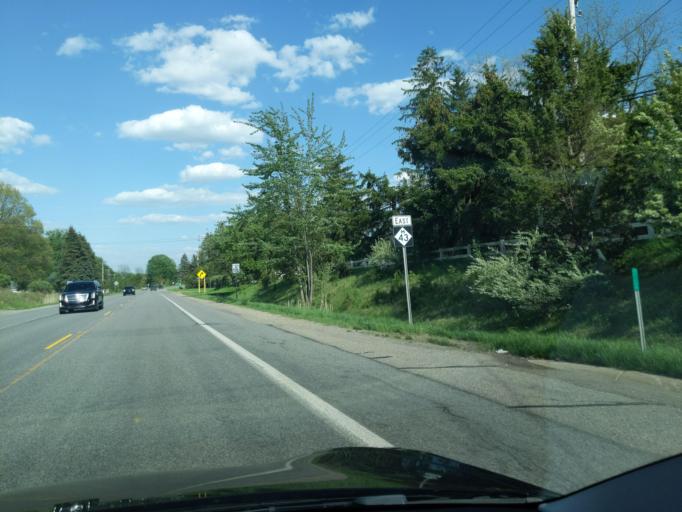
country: US
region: Michigan
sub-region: Eaton County
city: Grand Ledge
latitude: 42.7554
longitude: -84.7791
